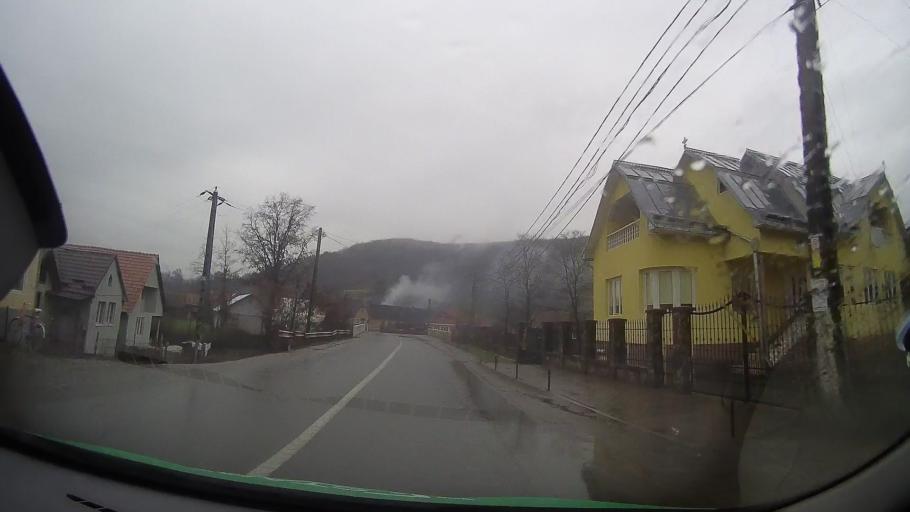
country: RO
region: Bistrita-Nasaud
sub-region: Comuna Sieut
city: Sieut
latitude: 46.9769
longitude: 24.6473
